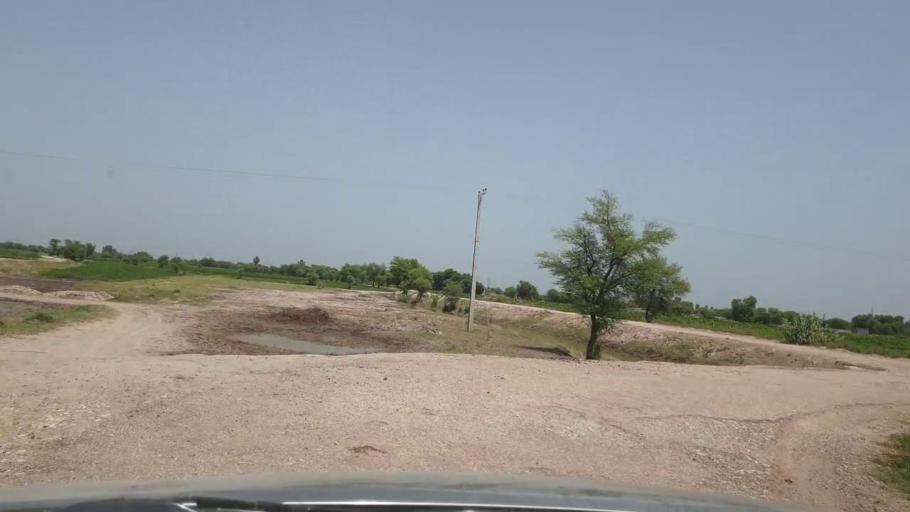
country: PK
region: Sindh
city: Pano Aqil
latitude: 27.8307
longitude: 69.2014
